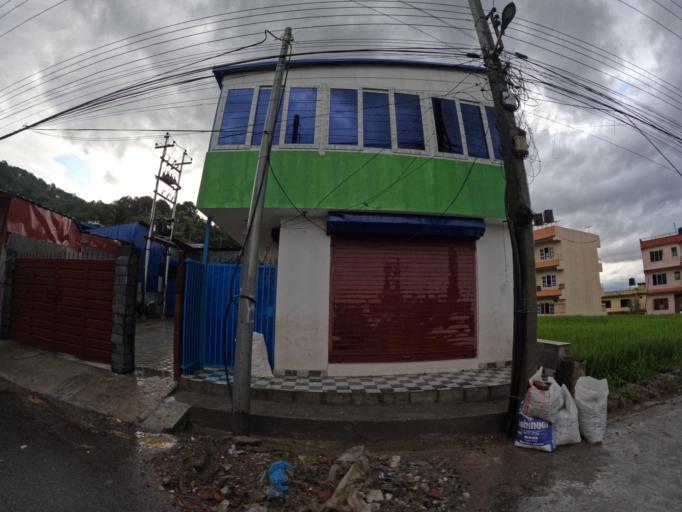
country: NP
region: Central Region
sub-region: Bagmati Zone
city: Kathmandu
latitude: 27.7764
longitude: 85.3388
